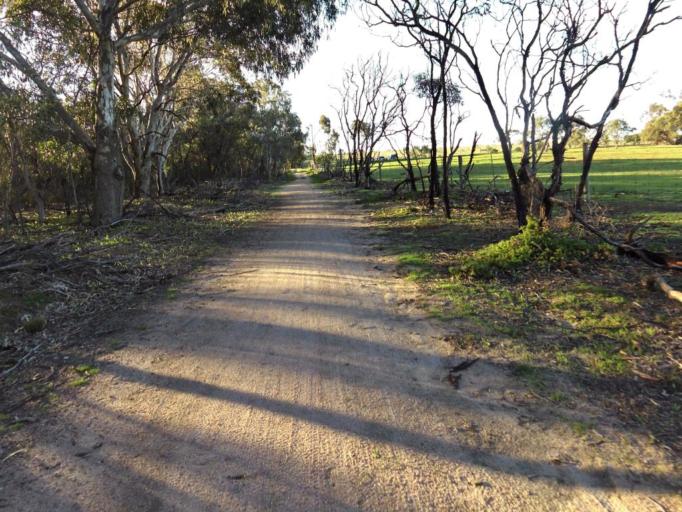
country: AU
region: Victoria
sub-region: Wyndham
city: Little River
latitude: -37.9560
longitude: 144.4455
